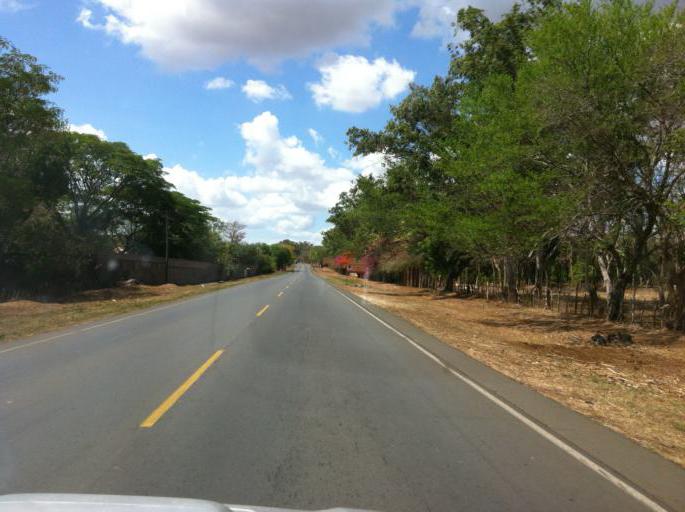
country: NI
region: Masaya
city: Nindiri
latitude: 12.0313
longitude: -86.1006
